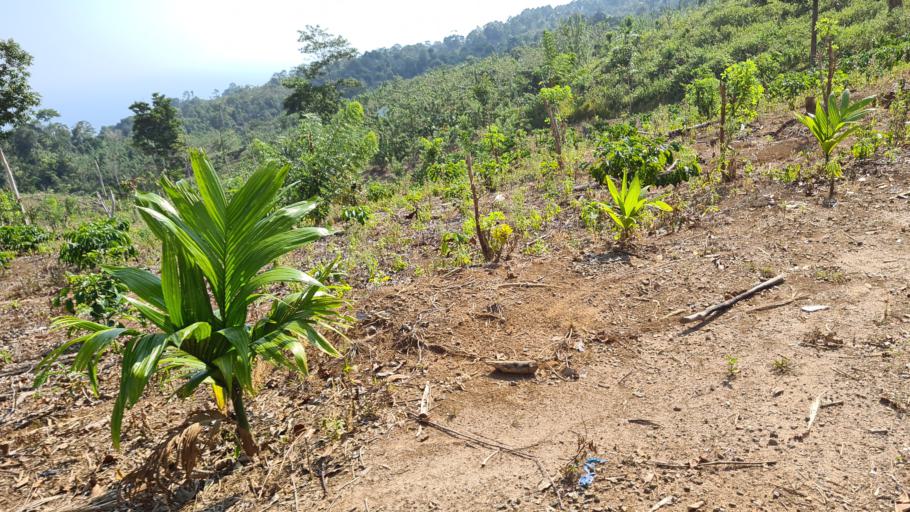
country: ID
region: Lampung
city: Kuripan
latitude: -5.0685
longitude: 103.8661
